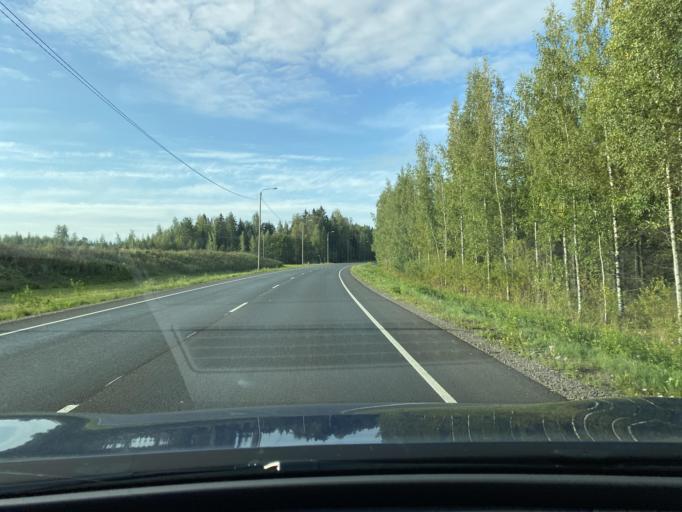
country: FI
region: Kymenlaakso
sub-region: Kouvola
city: Kouvola
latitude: 60.8869
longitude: 26.6045
